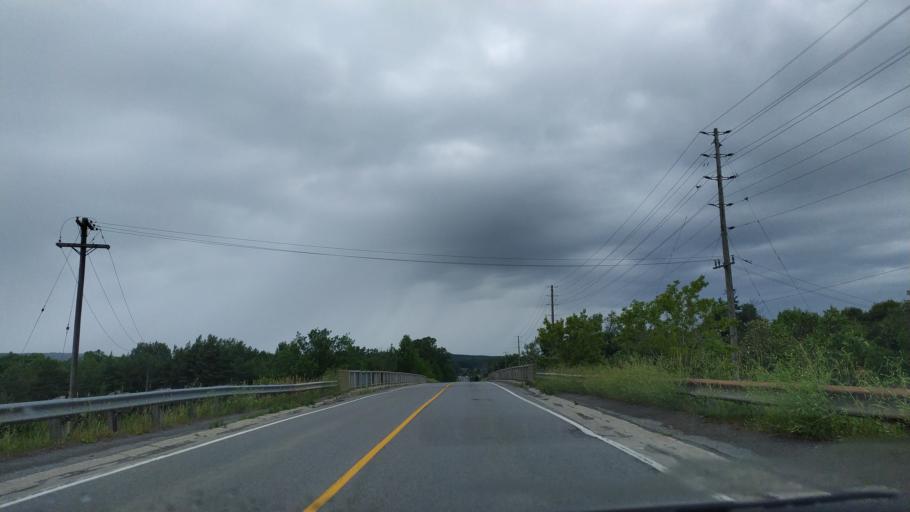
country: CA
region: Ontario
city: Quinte West
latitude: 44.0985
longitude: -77.6159
